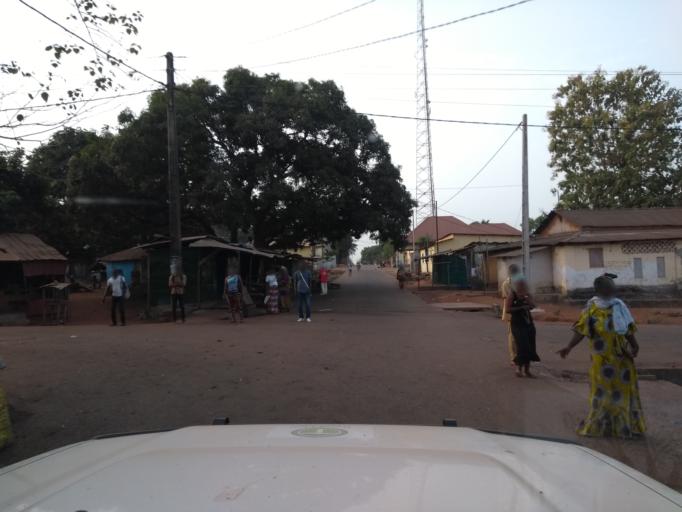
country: GN
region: Kindia
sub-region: Prefecture de Dubreka
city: Dubreka
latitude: 9.7902
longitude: -13.5231
